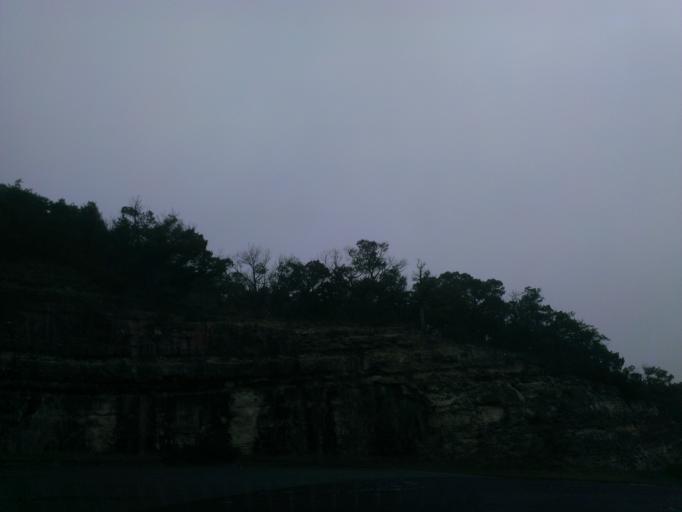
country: US
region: Texas
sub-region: Williamson County
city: Jollyville
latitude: 30.3734
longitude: -97.7916
